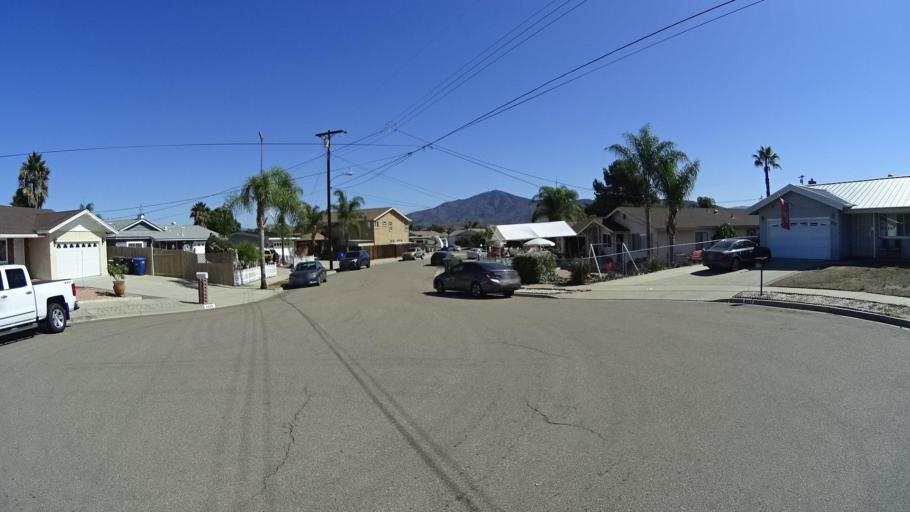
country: US
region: California
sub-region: San Diego County
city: La Presa
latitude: 32.6967
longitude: -117.0087
